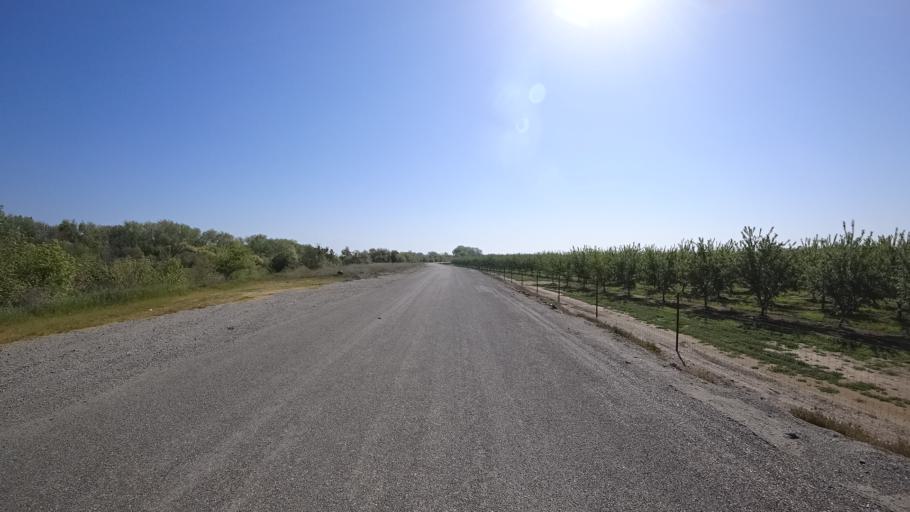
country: US
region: California
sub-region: Glenn County
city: Hamilton City
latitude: 39.6594
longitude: -121.9940
